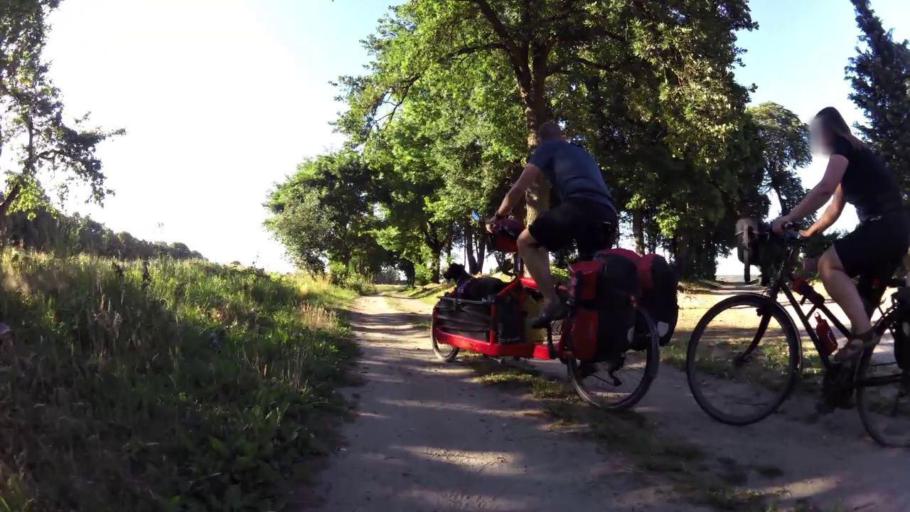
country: PL
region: West Pomeranian Voivodeship
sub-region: Powiat swidwinski
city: Swidwin
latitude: 53.7003
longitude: 15.8234
